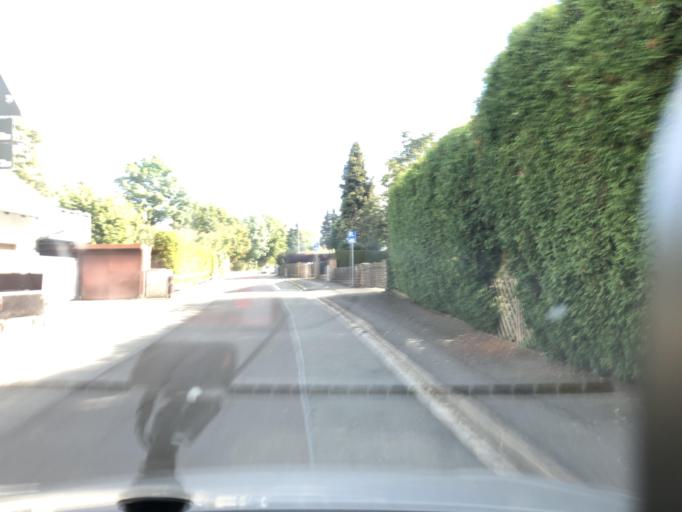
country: DE
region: Bavaria
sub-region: Regierungsbezirk Mittelfranken
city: Langenzenn
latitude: 49.4974
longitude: 10.8067
